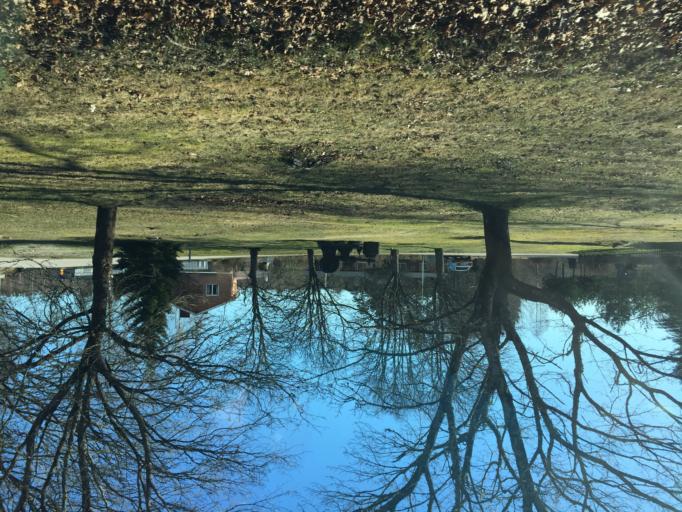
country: SE
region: OEstergoetland
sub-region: Finspangs Kommun
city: Finspang
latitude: 58.8462
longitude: 15.6986
